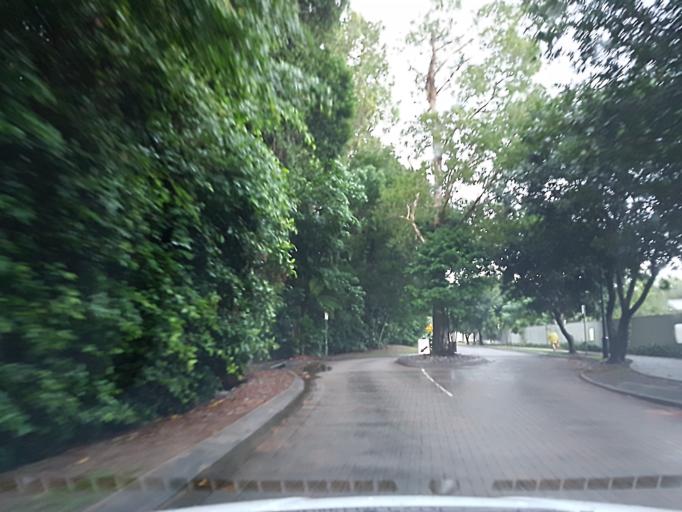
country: AU
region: Queensland
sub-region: Cairns
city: Palm Cove
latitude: -16.7523
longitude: 145.6699
